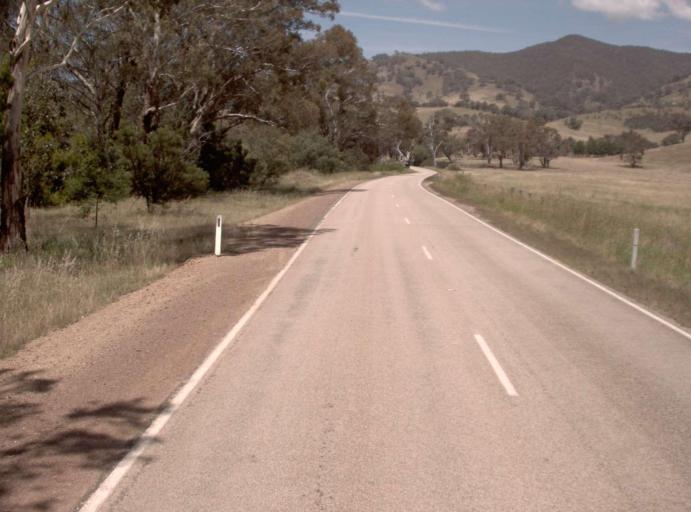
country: AU
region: Victoria
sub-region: East Gippsland
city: Bairnsdale
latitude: -37.2825
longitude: 147.7393
